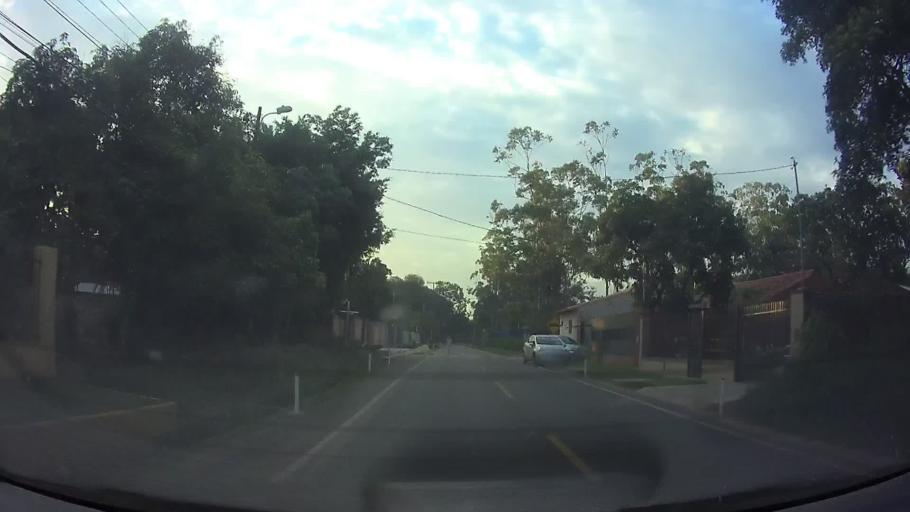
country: PY
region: Central
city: Limpio
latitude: -25.2503
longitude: -57.5016
